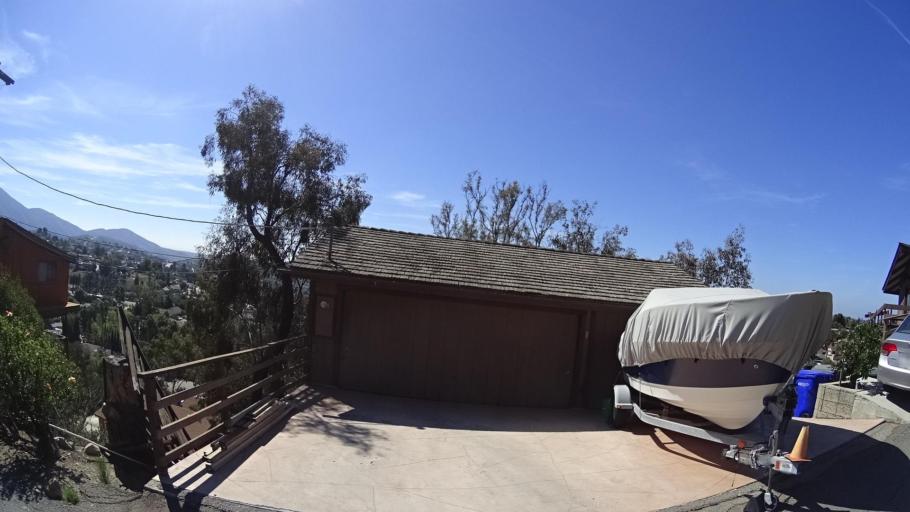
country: US
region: California
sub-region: San Diego County
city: Casa de Oro-Mount Helix
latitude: 32.7571
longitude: -116.9722
